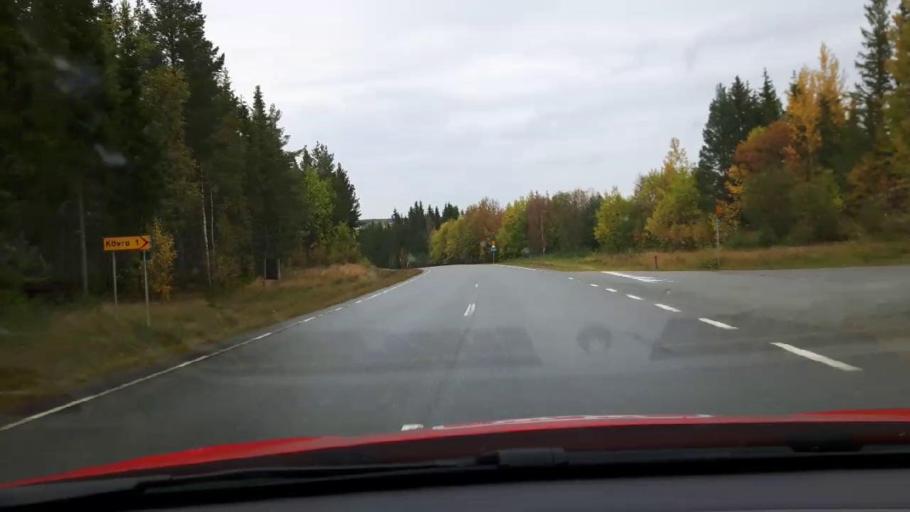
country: SE
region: Jaemtland
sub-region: Bergs Kommun
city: Hoverberg
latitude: 62.9226
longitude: 14.3350
